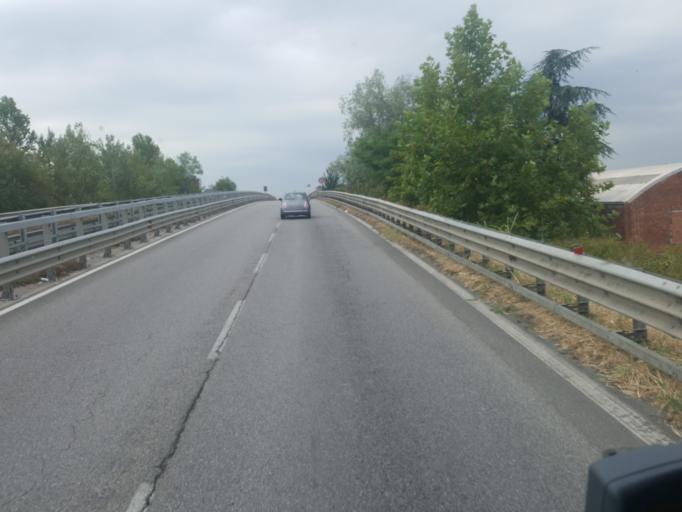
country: IT
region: Lombardy
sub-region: Citta metropolitana di Milano
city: Melzo
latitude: 45.5026
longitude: 9.4142
